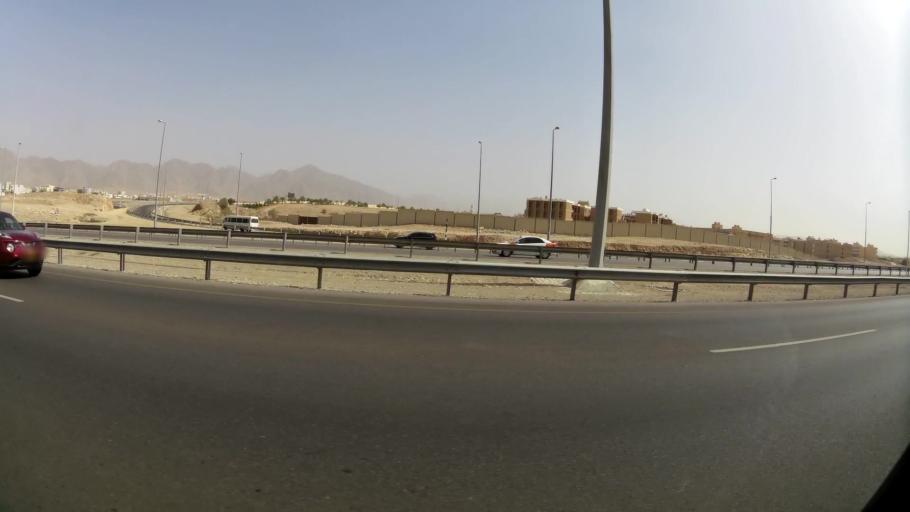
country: OM
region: Muhafazat Masqat
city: Bawshar
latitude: 23.5675
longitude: 58.3761
